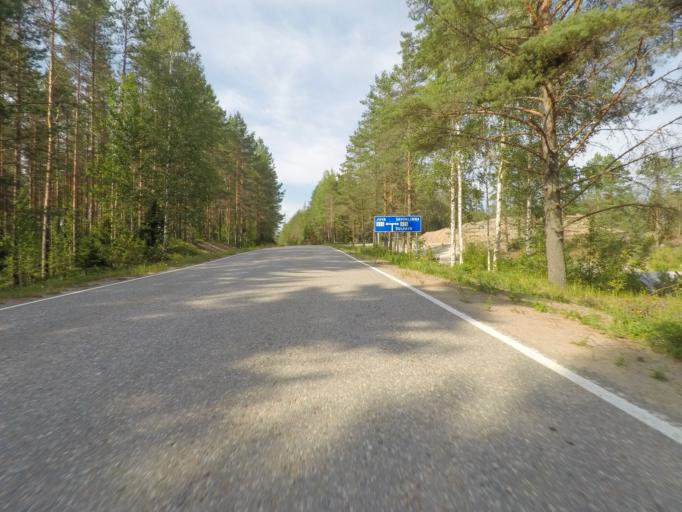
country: FI
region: Southern Savonia
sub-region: Savonlinna
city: Sulkava
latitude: 61.7875
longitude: 28.2432
